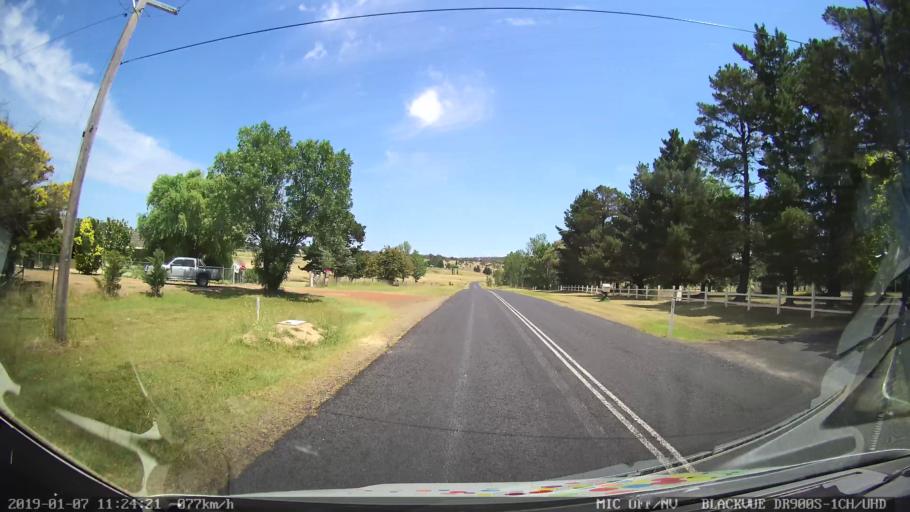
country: AU
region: New South Wales
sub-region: Armidale Dumaresq
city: Armidale
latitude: -30.4676
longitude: 151.6127
